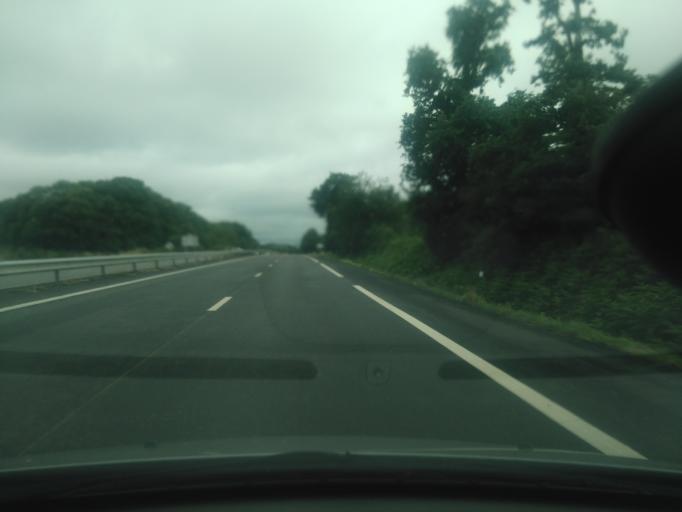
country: FR
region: Brittany
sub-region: Departement d'Ille-et-Vilaine
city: Saint-Pierre-de-Plesguen
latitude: 48.4233
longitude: -1.9115
